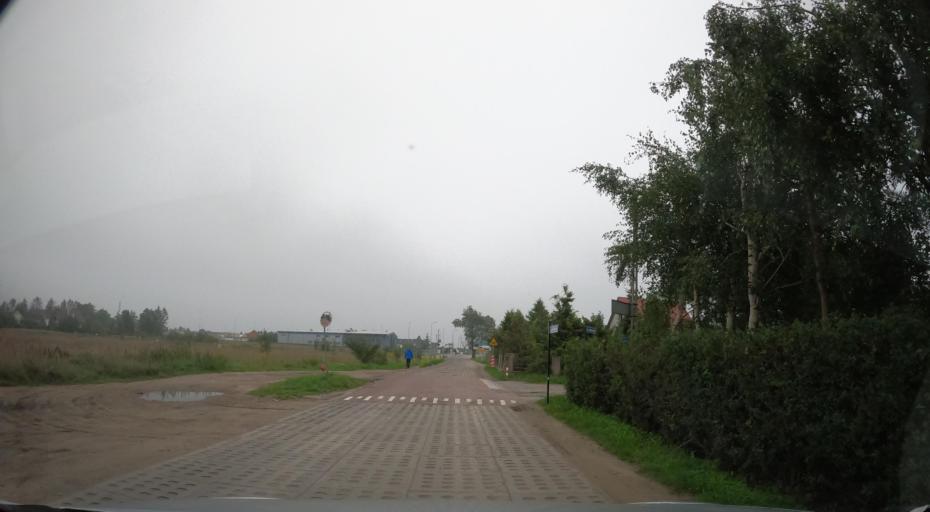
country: PL
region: Pomeranian Voivodeship
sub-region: Powiat kartuski
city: Chwaszczyno
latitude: 54.4184
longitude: 18.4469
